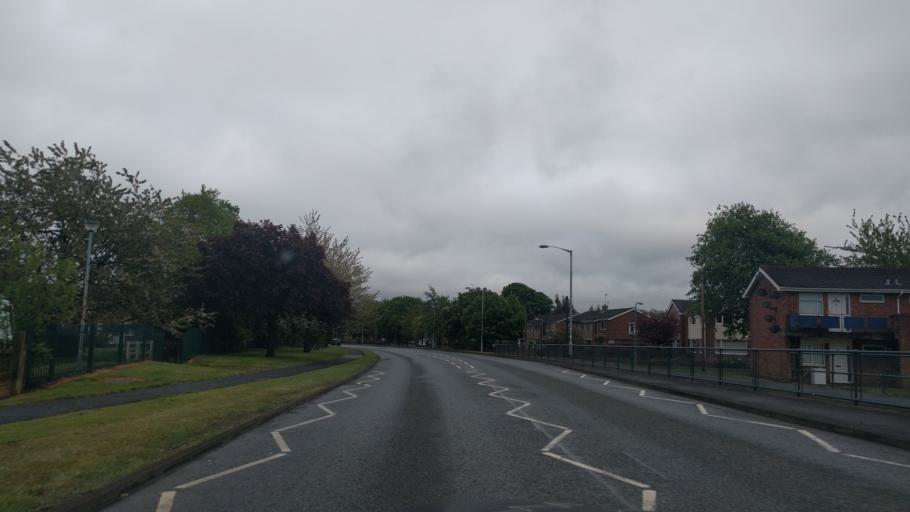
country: GB
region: England
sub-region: Northumberland
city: Morpeth
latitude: 55.1591
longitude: -1.6813
